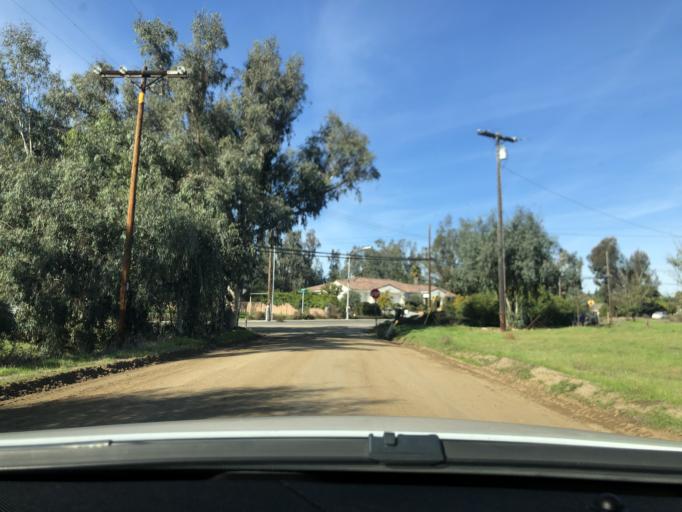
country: US
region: California
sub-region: San Diego County
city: Escondido
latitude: 33.0884
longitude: -117.0894
